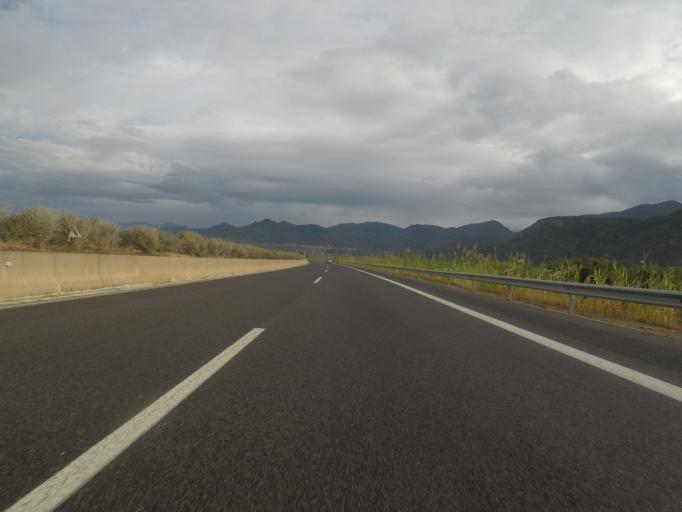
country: GR
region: Peloponnese
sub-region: Nomos Messinias
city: Arfara
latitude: 37.1256
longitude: 22.0394
